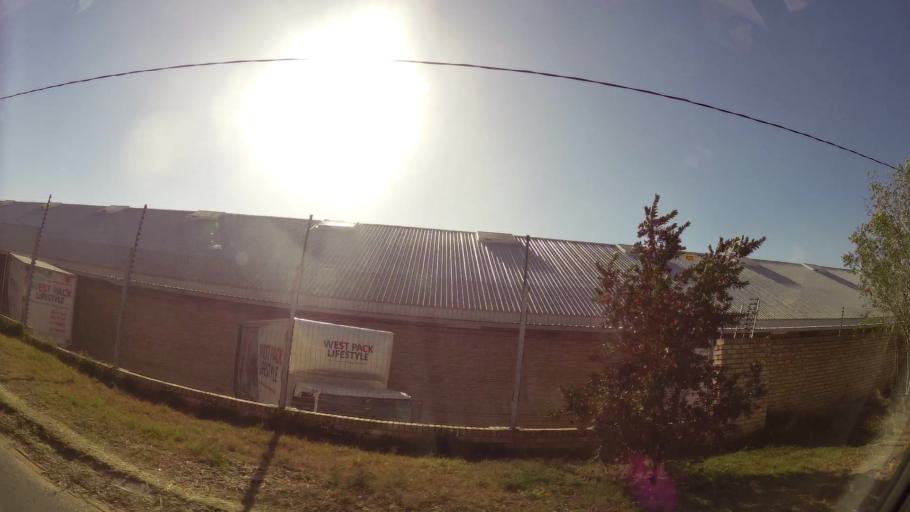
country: ZA
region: Gauteng
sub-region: City of Johannesburg Metropolitan Municipality
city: Diepsloot
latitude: -26.0096
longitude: 27.9460
